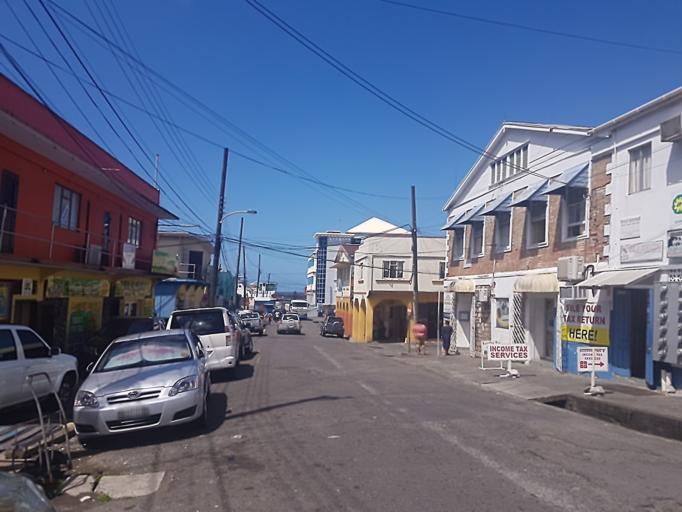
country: VC
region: Saint George
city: Kingstown
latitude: 13.1516
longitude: -61.2225
